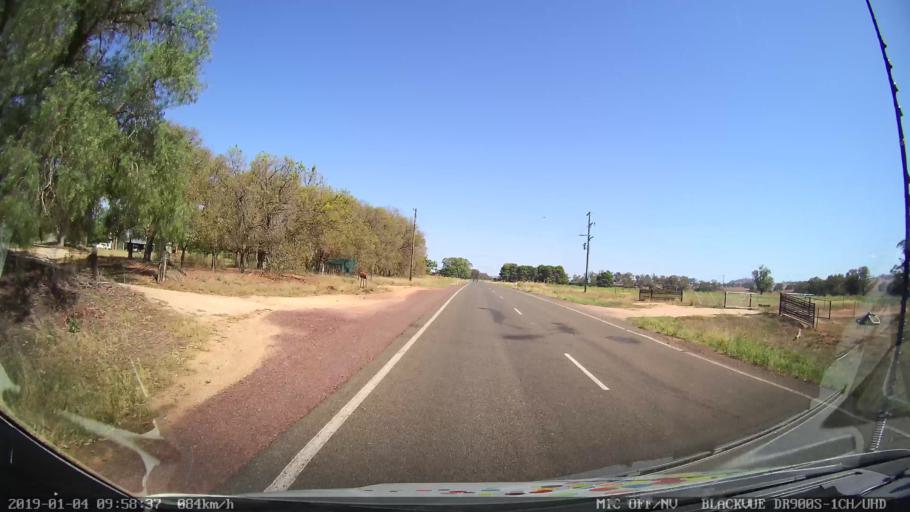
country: AU
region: New South Wales
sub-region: Cabonne
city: Canowindra
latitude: -33.5166
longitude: 148.3930
